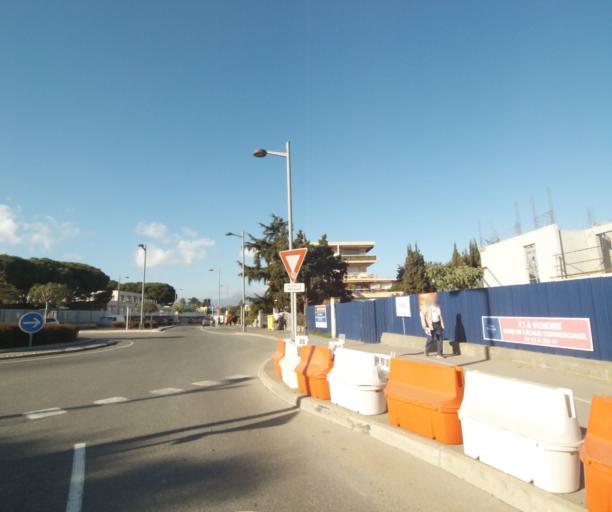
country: FR
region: Provence-Alpes-Cote d'Azur
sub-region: Departement des Alpes-Maritimes
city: Antibes
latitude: 43.5924
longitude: 7.1159
